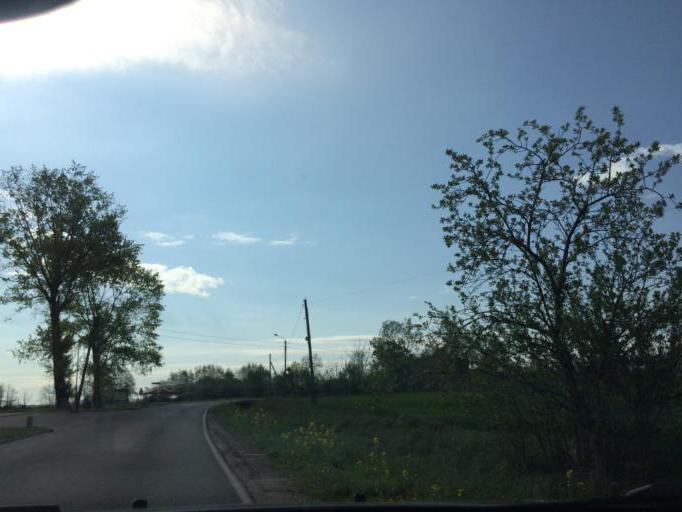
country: PL
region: Lower Silesian Voivodeship
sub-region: Powiat dzierzoniowski
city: Pieszyce
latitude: 50.7325
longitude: 16.5620
